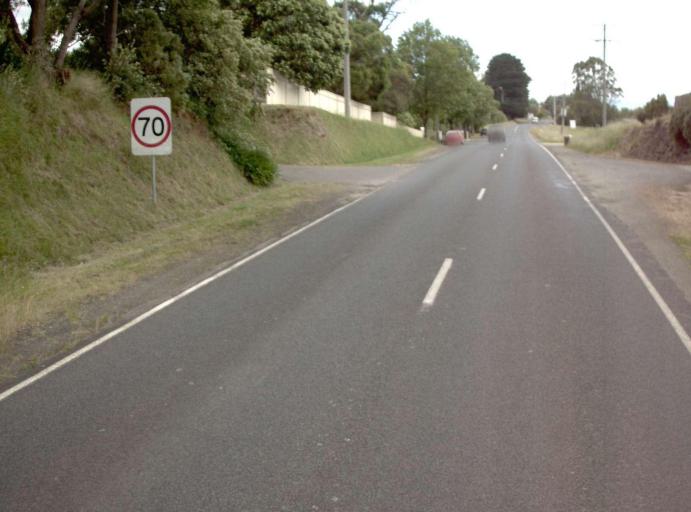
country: AU
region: Victoria
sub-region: Baw Baw
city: Warragul
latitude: -38.1354
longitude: 145.9338
